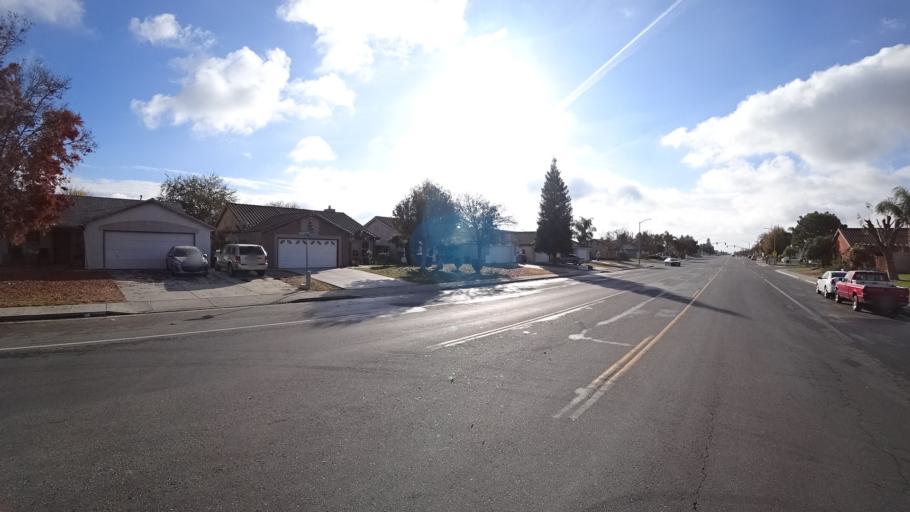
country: US
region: California
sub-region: Kern County
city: Greenfield
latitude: 35.2909
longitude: -119.0119
